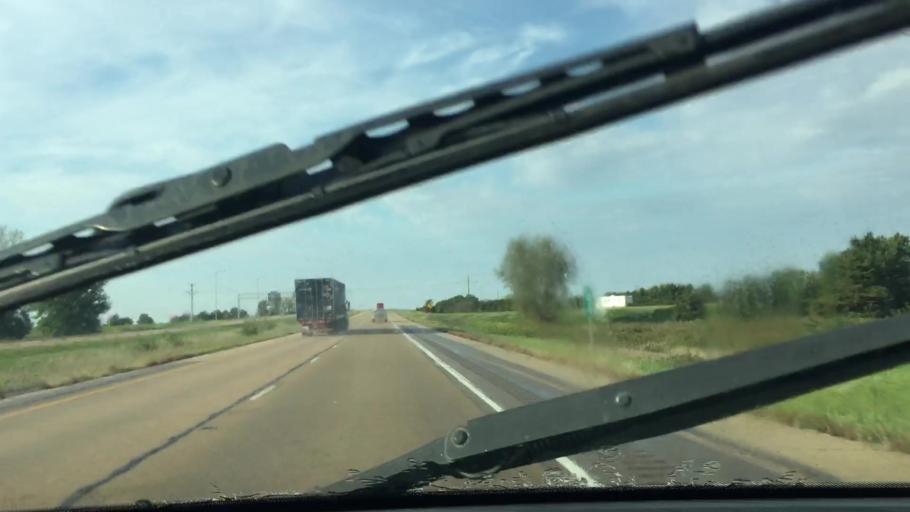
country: US
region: Illinois
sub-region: Whiteside County
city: Rock Falls
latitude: 41.7577
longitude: -89.6379
